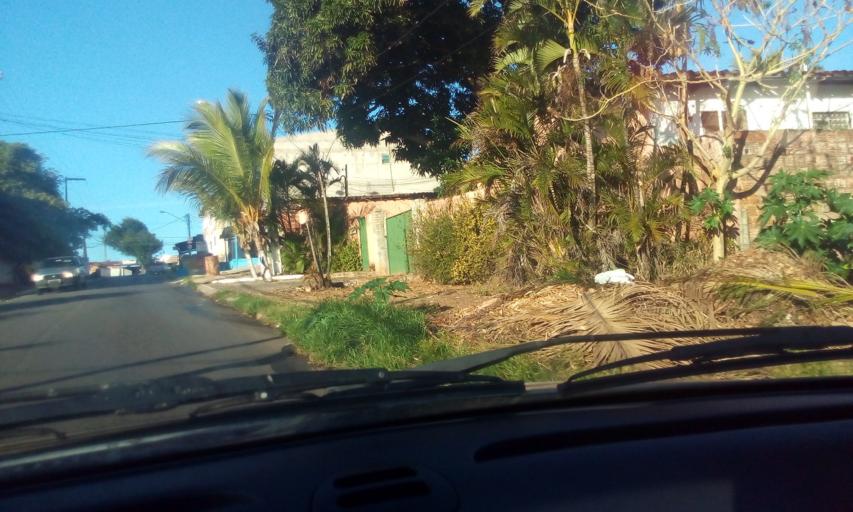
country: BR
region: Rio Grande do Norte
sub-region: Parnamirim
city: Parnamirim
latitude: -5.9508
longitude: -35.1622
